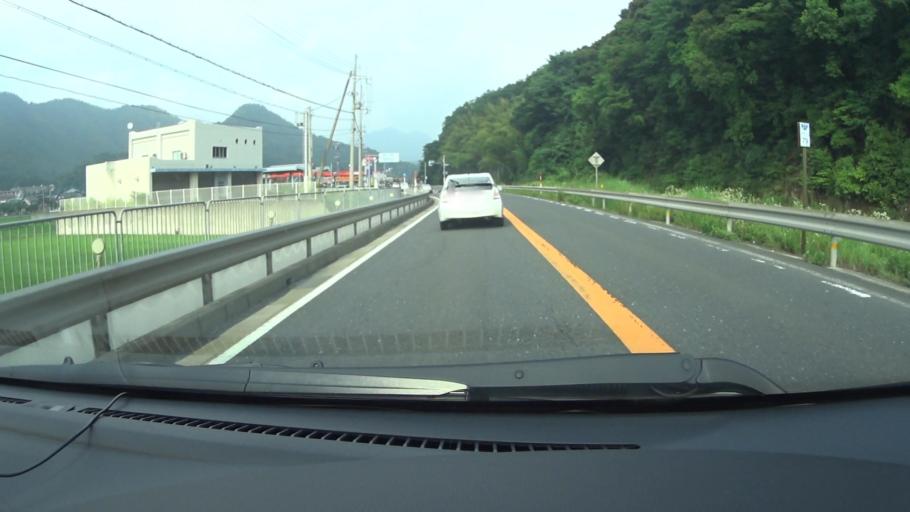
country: JP
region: Kyoto
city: Maizuru
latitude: 35.4794
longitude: 135.4126
